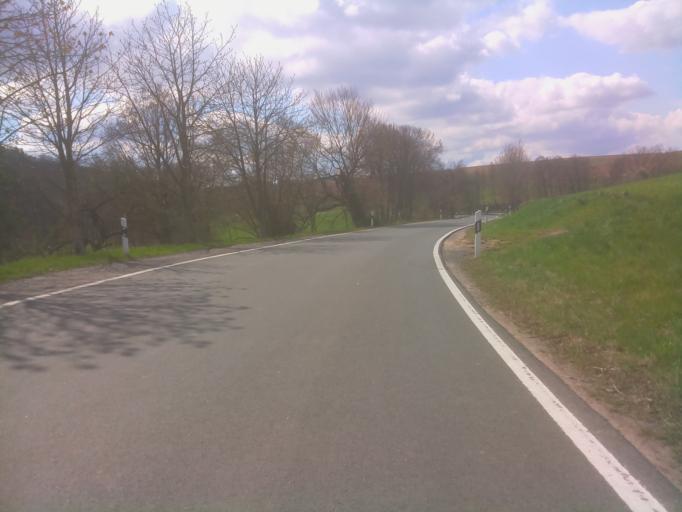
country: DE
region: Thuringia
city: Karlsdorf
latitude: 50.7910
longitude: 11.8015
